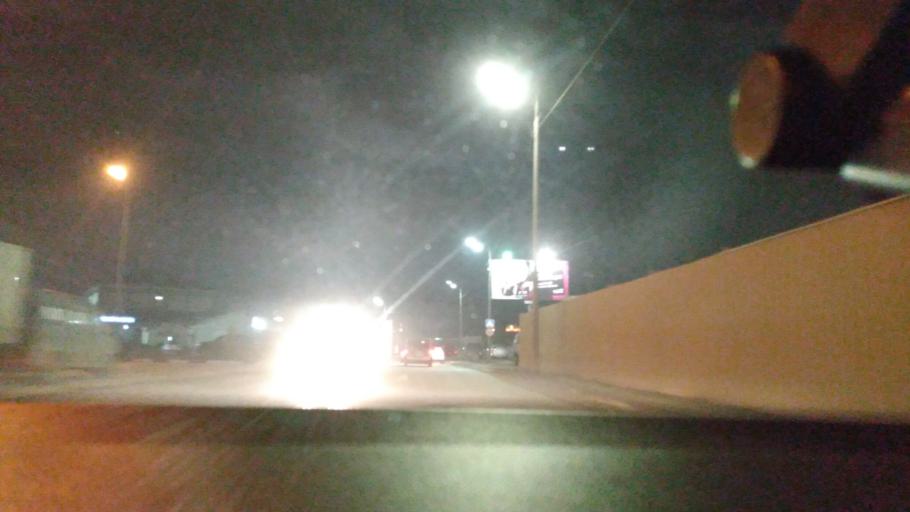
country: RU
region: Moskovskaya
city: Balashikha
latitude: 55.8168
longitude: 37.9530
